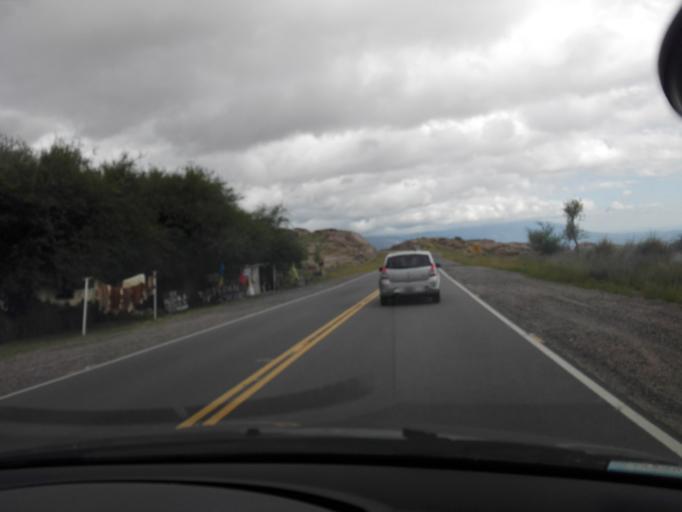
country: AR
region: Cordoba
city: Mina Clavero
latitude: -31.6351
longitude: -64.9081
